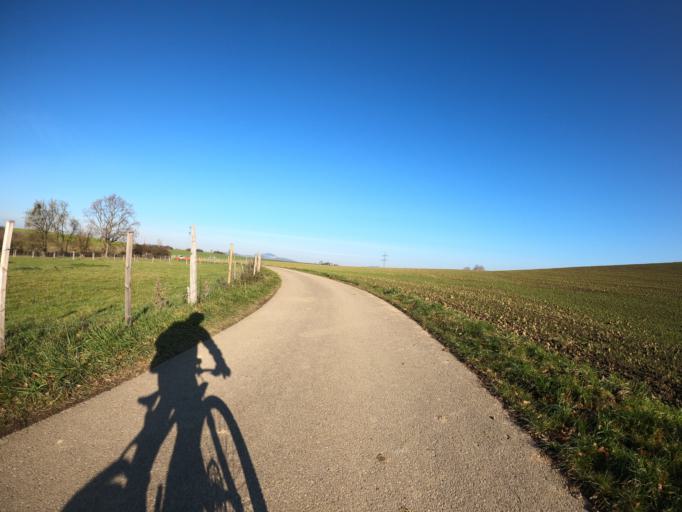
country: DE
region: Baden-Wuerttemberg
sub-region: Regierungsbezirk Stuttgart
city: Eschenbach
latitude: 48.6679
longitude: 9.6724
